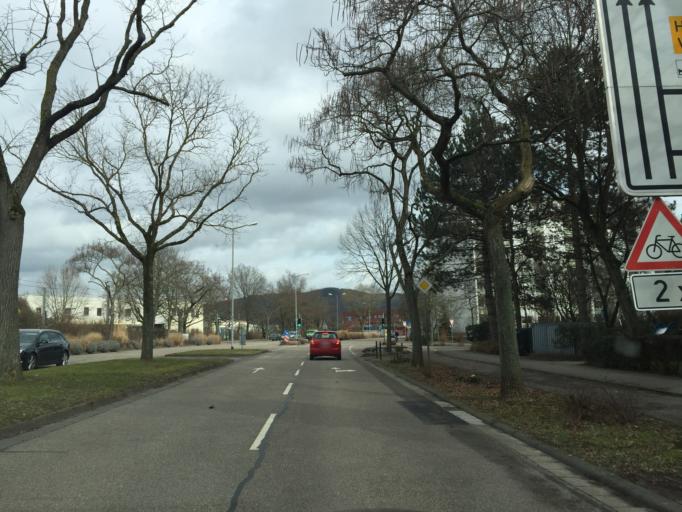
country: DE
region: Baden-Wuerttemberg
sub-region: Karlsruhe Region
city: Weinheim
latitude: 49.5464
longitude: 8.6516
